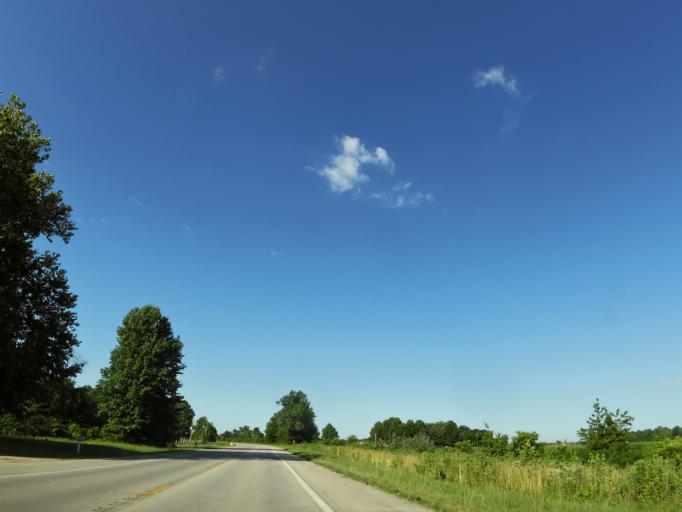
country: US
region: Arkansas
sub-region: Clay County
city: Corning
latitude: 36.5302
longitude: -90.5365
